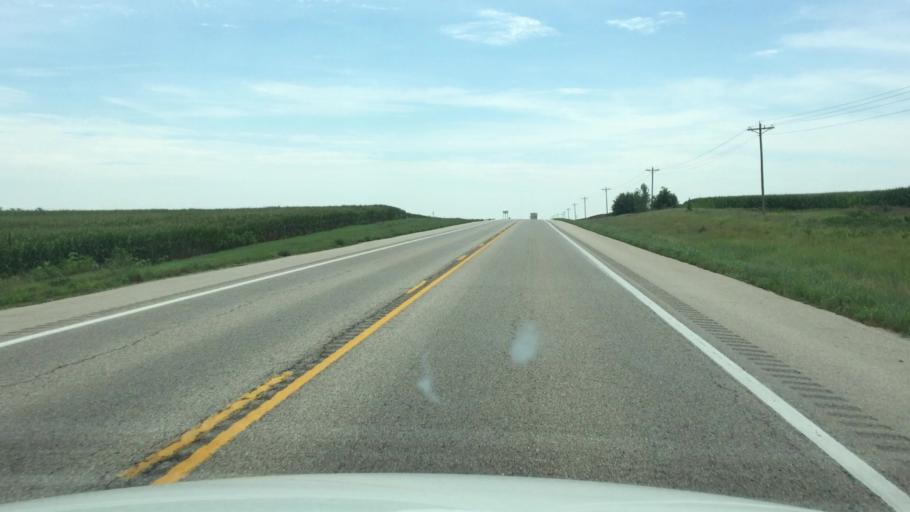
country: US
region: Kansas
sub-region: Nemaha County
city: Sabetha
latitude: 39.7170
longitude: -95.7300
